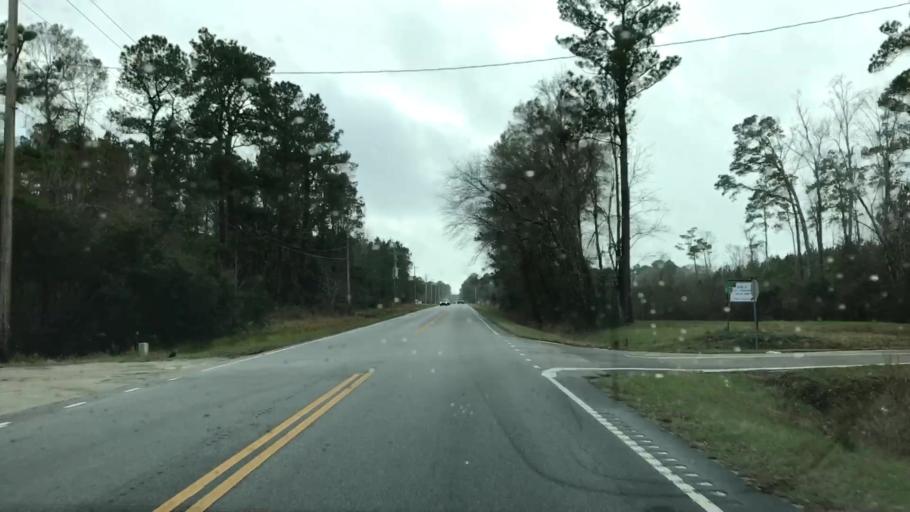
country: US
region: South Carolina
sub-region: Horry County
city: Socastee
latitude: 33.7397
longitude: -79.0808
